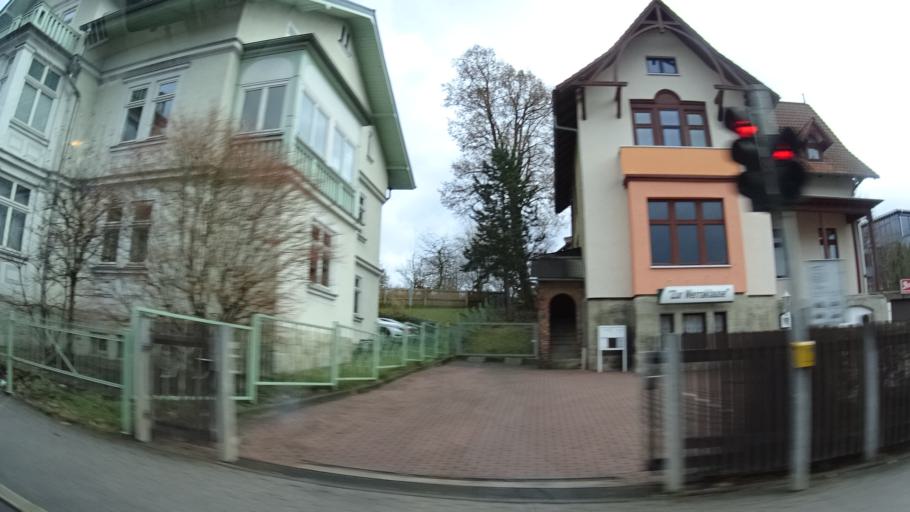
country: DE
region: Thuringia
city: Meiningen
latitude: 50.5684
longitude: 10.4189
